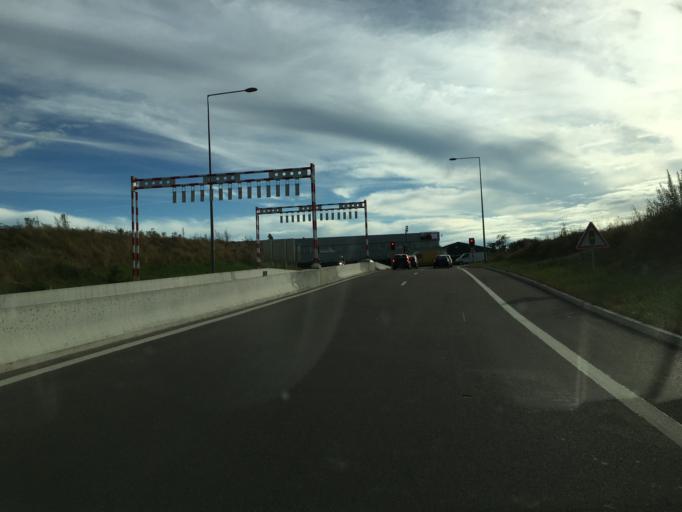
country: FR
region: Bourgogne
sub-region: Departement de la Cote-d'Or
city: Daix
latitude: 47.3455
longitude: 4.9983
